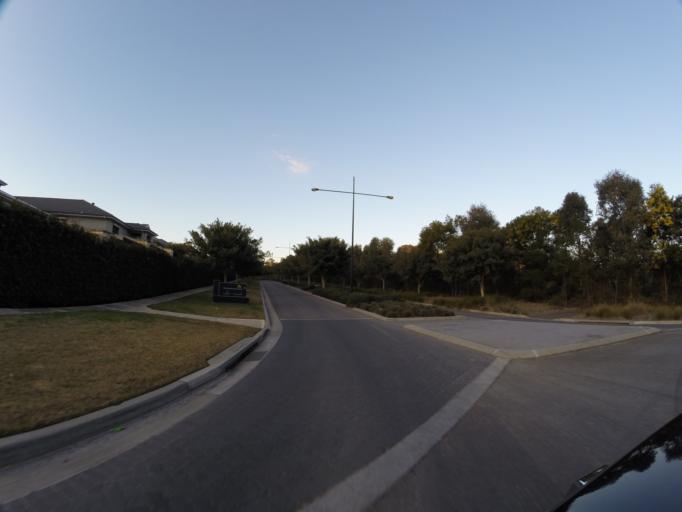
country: AU
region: New South Wales
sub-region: Camden
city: Narellan
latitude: -34.0204
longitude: 150.7400
